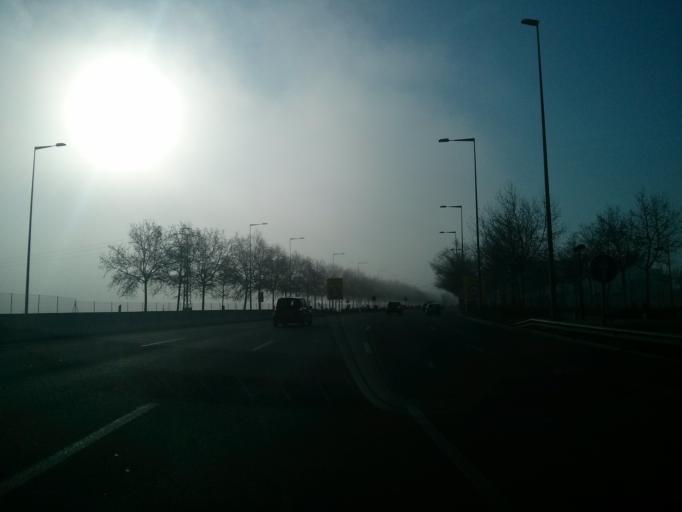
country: ES
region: Valencia
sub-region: Provincia de Valencia
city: Tavernes Blanques
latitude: 39.5025
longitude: -0.3916
